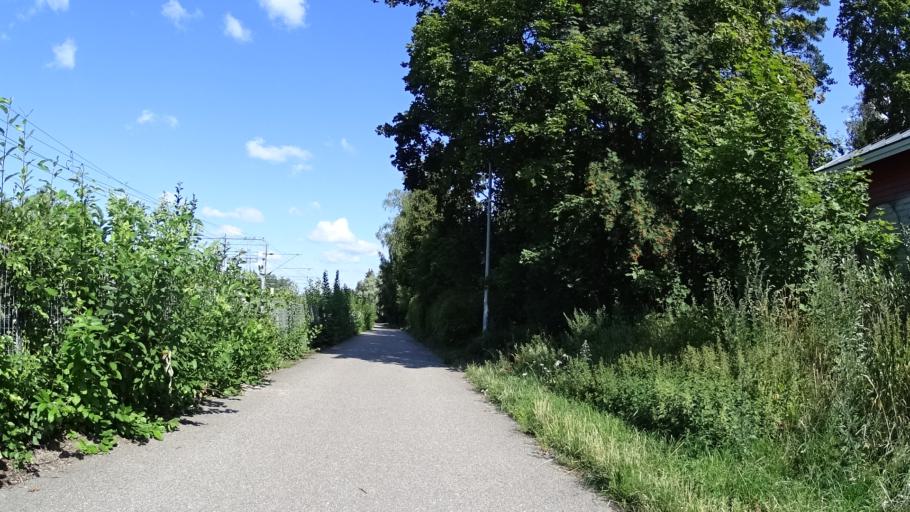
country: FI
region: Uusimaa
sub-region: Helsinki
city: Jaervenpaeae
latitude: 60.4666
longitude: 25.0991
